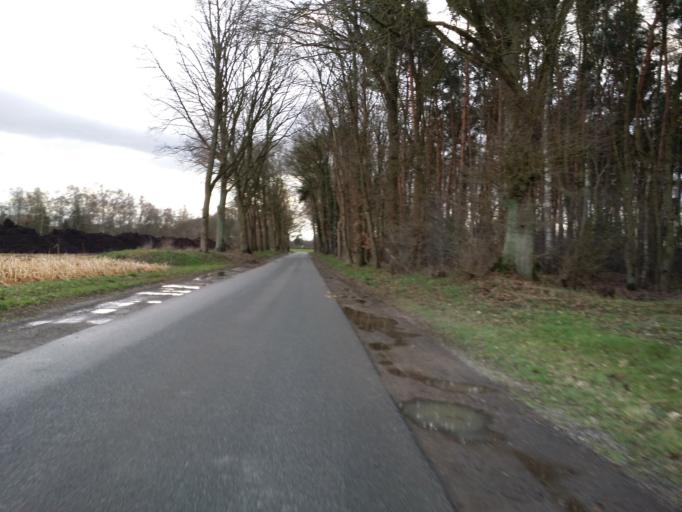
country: DE
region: Lower Saxony
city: Gross Ippener
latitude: 52.9907
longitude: 8.6364
